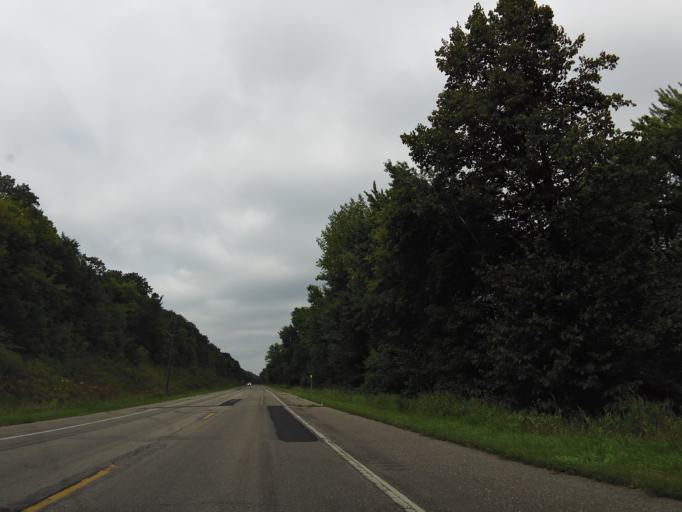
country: US
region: Minnesota
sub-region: Chippewa County
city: Montevideo
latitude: 44.8796
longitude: -95.6489
